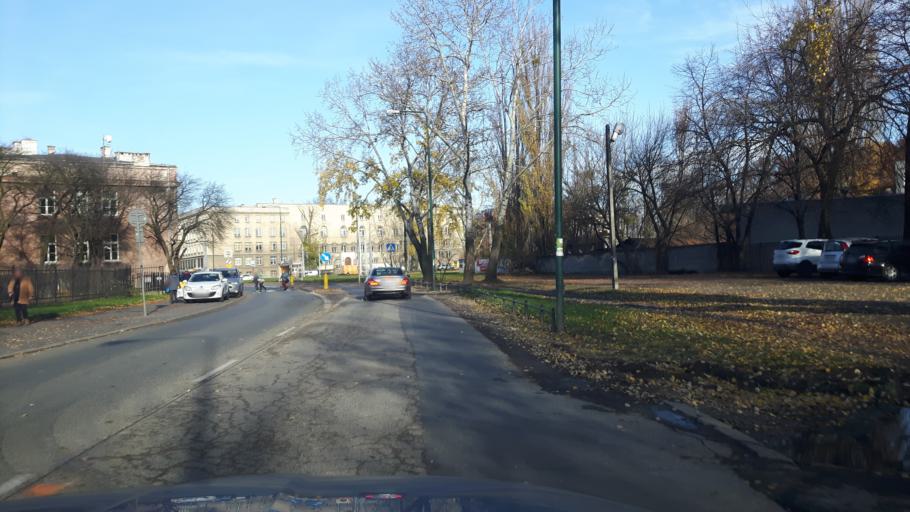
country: PL
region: Masovian Voivodeship
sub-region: Warszawa
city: Ochota
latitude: 52.2090
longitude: 20.9800
